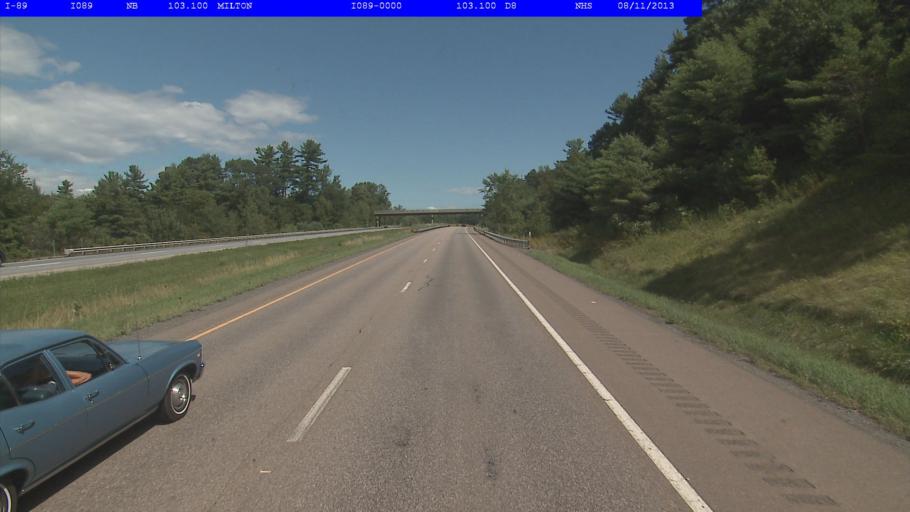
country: US
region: Vermont
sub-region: Chittenden County
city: Milton
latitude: 44.6580
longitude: -73.1384
